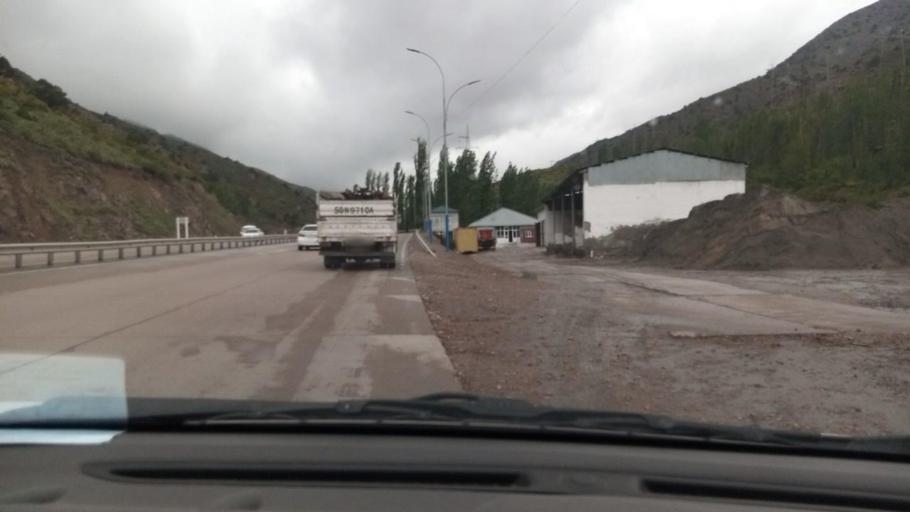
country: TJ
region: Viloyati Sughd
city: Shaydon
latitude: 41.0390
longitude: 70.5792
